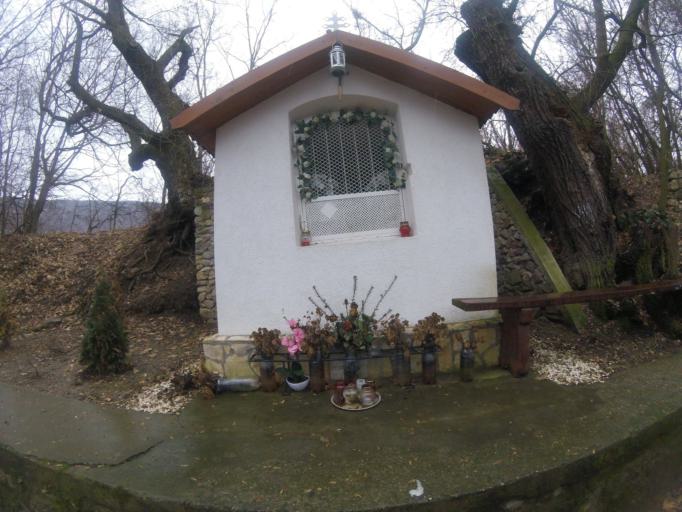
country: HU
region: Komarom-Esztergom
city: Kesztolc
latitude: 47.7110
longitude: 18.8038
